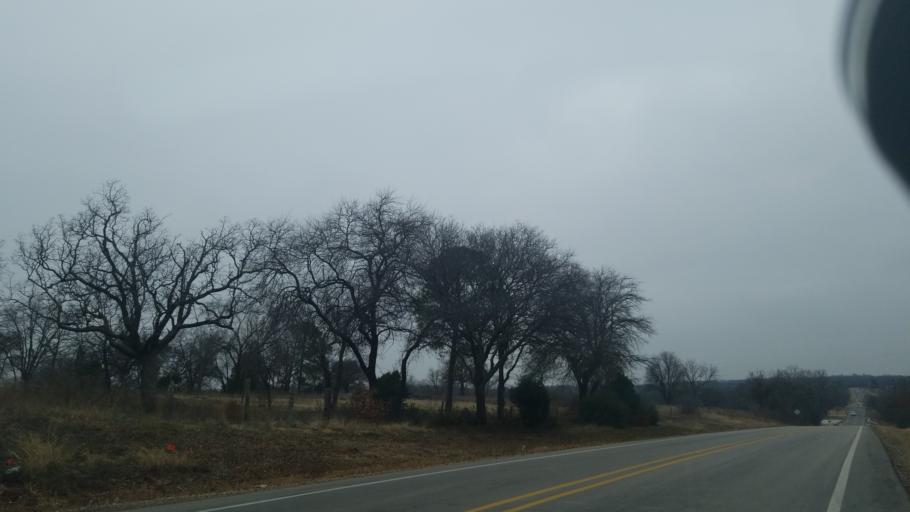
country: US
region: Texas
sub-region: Denton County
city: Argyle
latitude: 33.1177
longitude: -97.1396
